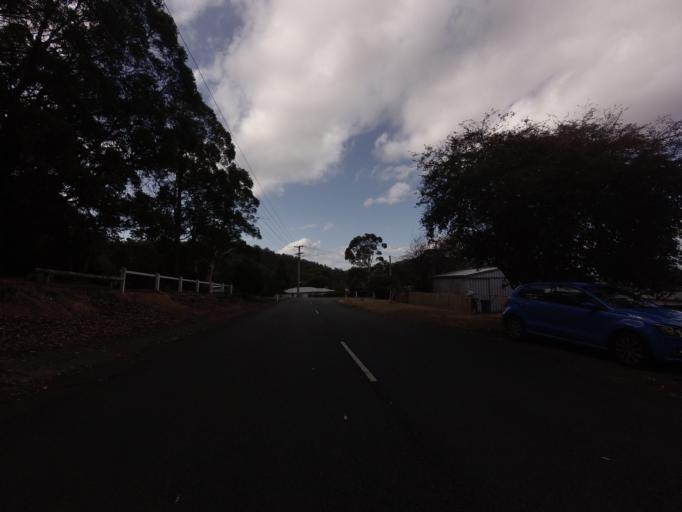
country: AU
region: Tasmania
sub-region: Hobart
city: Dynnyrne
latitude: -42.8999
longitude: 147.2748
